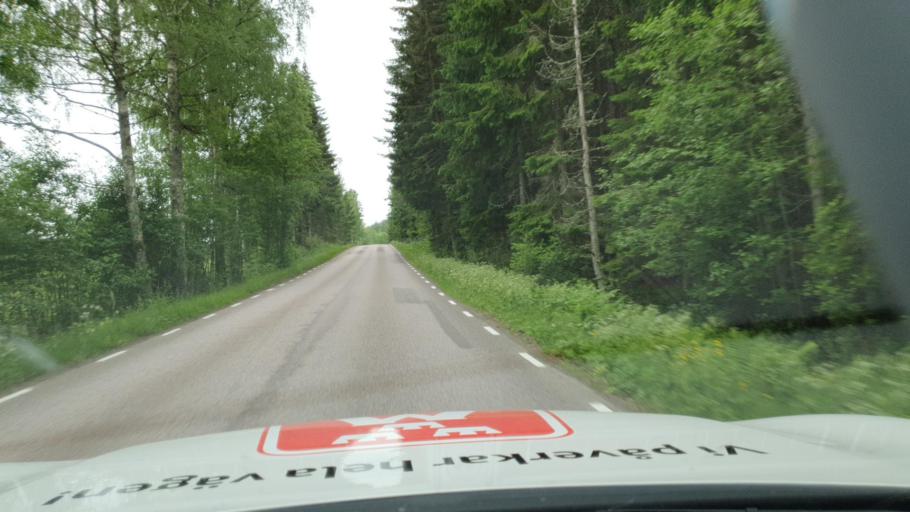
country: SE
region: Vaermland
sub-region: Kils Kommun
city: Kil
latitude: 59.6571
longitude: 13.3097
